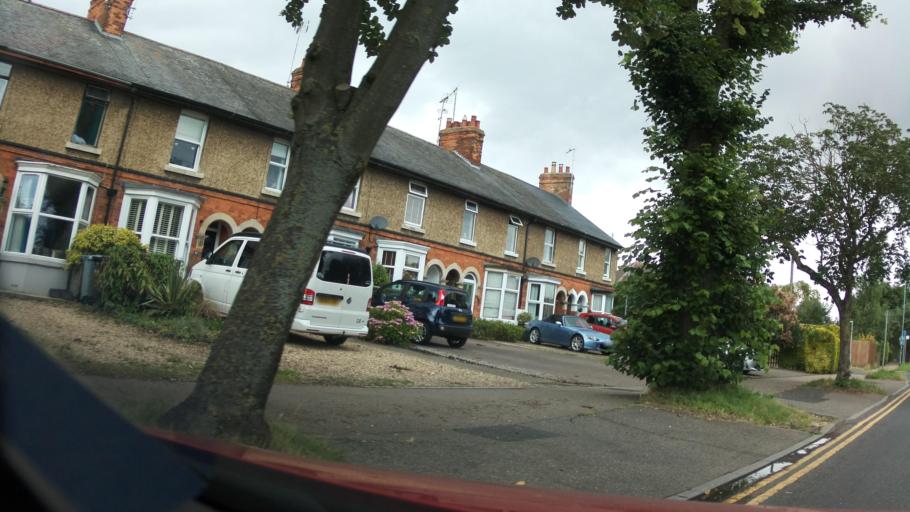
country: GB
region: England
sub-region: Lincolnshire
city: Stamford
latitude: 52.6609
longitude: -0.4662
